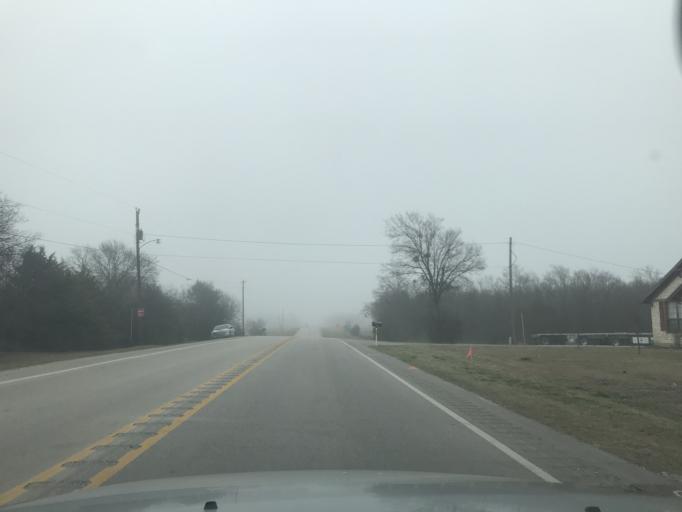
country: US
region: Texas
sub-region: Rockwall County
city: Royse City
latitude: 32.9952
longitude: -96.3077
